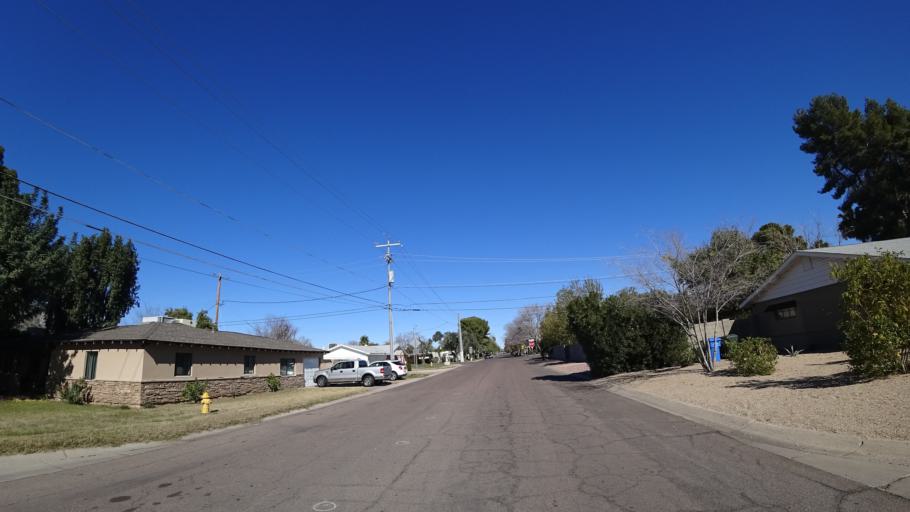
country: US
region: Arizona
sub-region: Maricopa County
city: Phoenix
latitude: 33.5158
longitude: -112.0606
